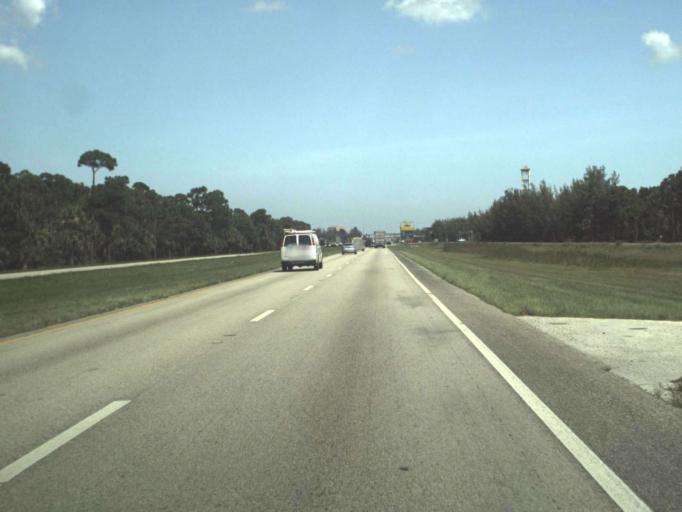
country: US
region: Florida
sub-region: Palm Beach County
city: Palm Beach Gardens
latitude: 26.8029
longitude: -80.1421
